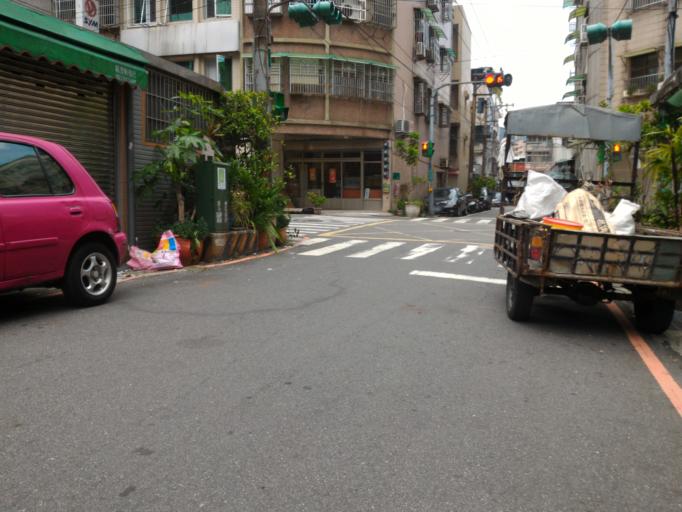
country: TW
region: Taipei
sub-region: Taipei
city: Banqiao
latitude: 24.9825
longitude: 121.4162
